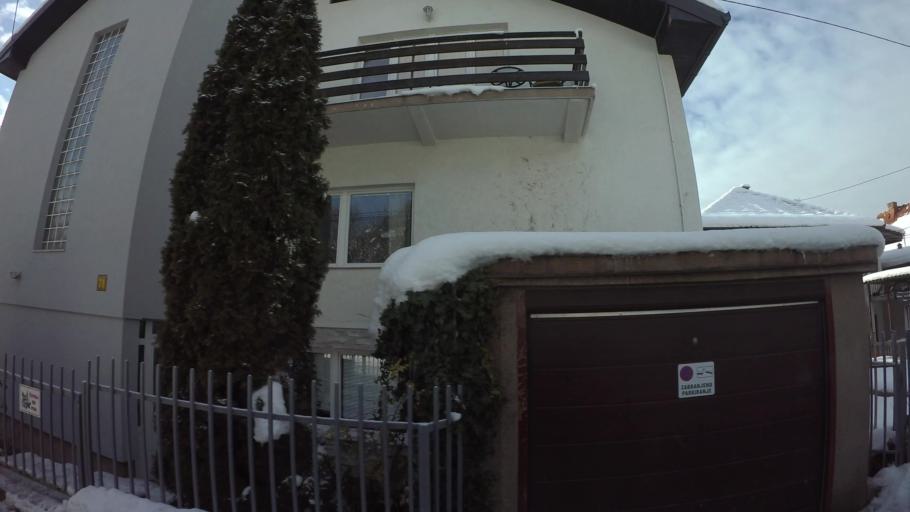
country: BA
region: Federation of Bosnia and Herzegovina
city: Kobilja Glava
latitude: 43.8732
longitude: 18.4197
